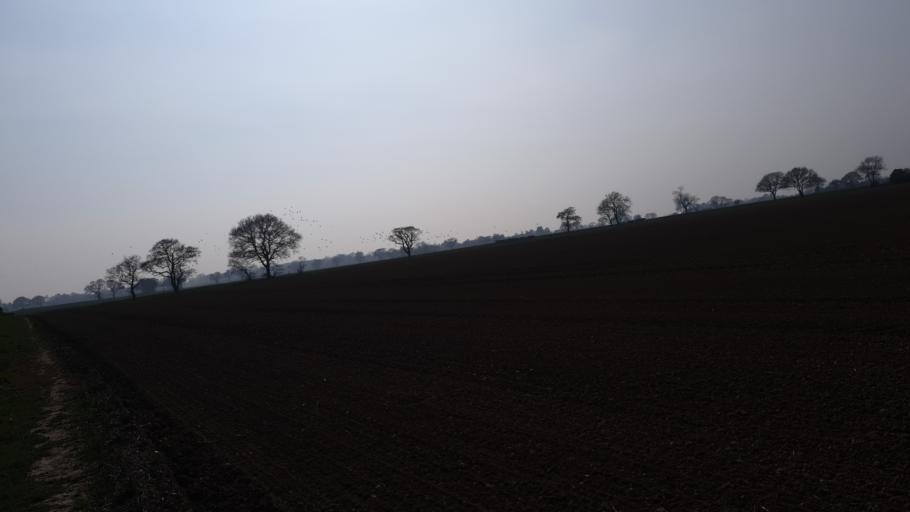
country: GB
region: England
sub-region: Essex
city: Mistley
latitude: 51.8963
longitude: 1.1221
